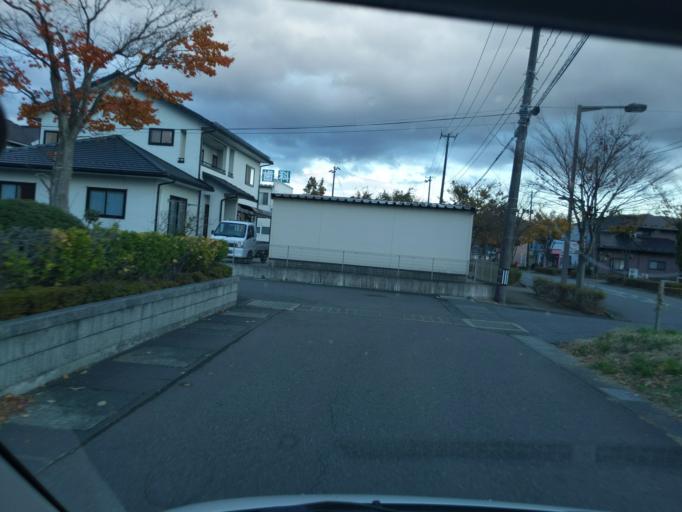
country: JP
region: Iwate
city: Mizusawa
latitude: 39.0506
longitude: 141.1280
